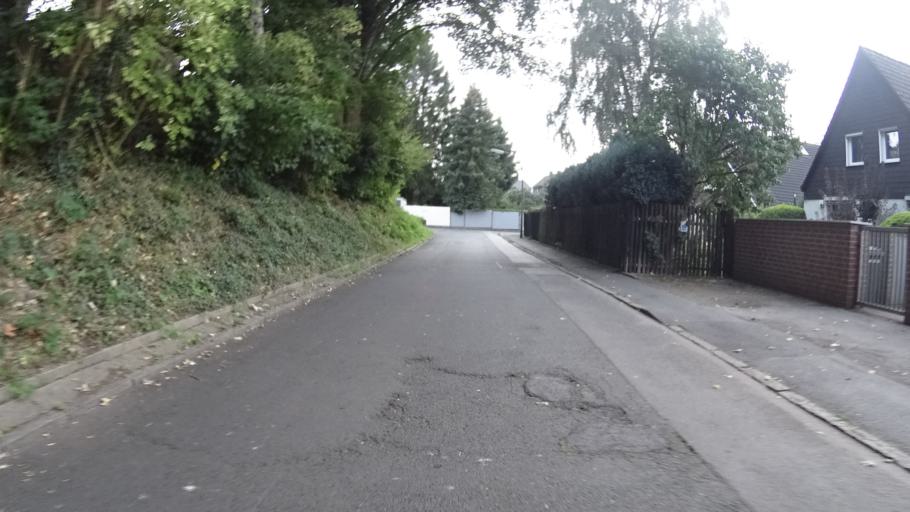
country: DE
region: North Rhine-Westphalia
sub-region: Regierungsbezirk Arnsberg
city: Dortmund
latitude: 51.4924
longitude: 7.4377
